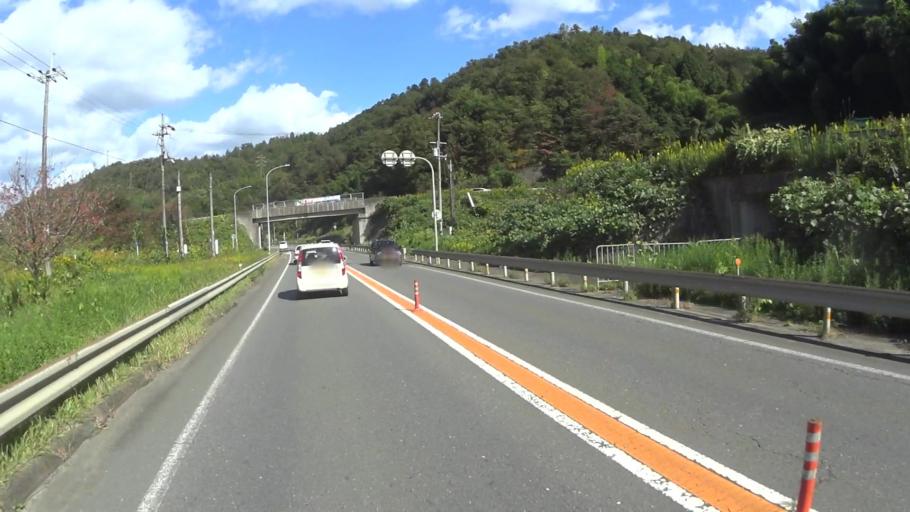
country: JP
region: Kyoto
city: Maizuru
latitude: 35.4122
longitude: 135.3314
